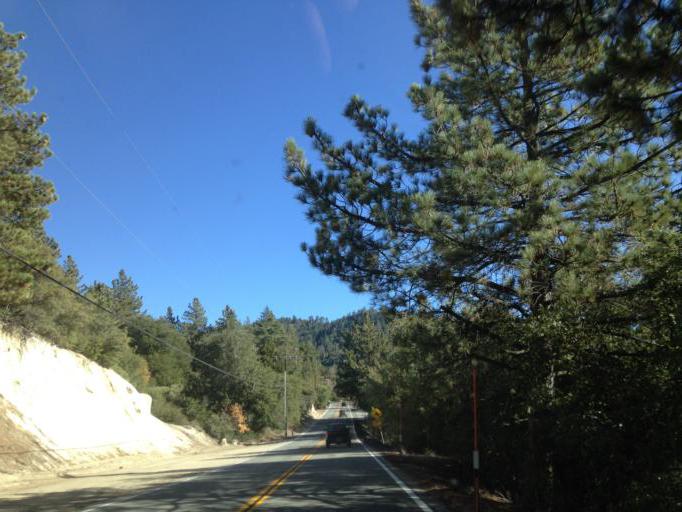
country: US
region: California
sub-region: Riverside County
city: Idyllwild-Pine Cove
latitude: 33.7803
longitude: -116.7466
